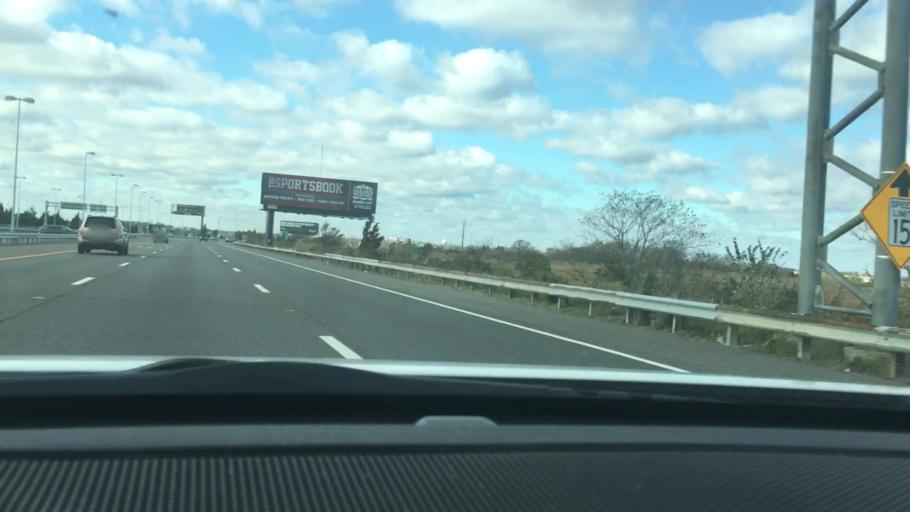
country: US
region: New Jersey
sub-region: Atlantic County
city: Pleasantville
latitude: 39.3849
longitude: -74.5014
